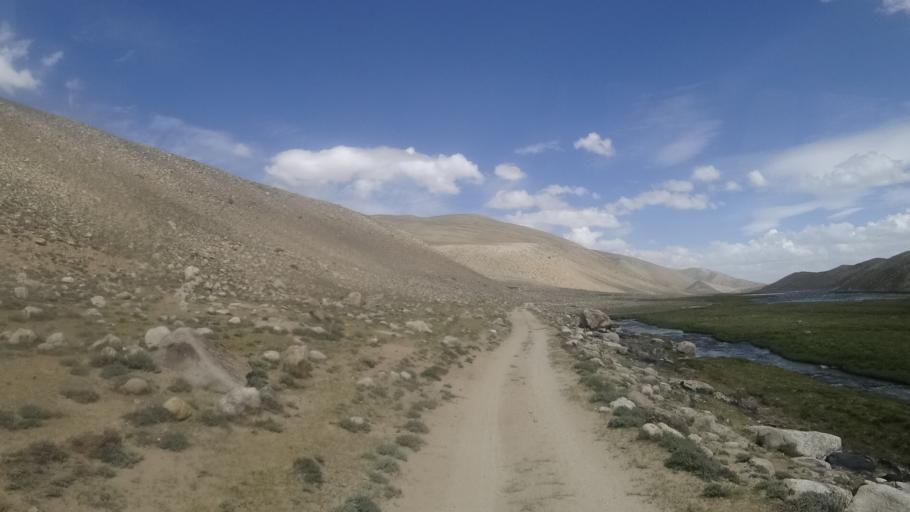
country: TJ
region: Gorno-Badakhshan
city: Murghob
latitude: 37.4745
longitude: 73.4519
